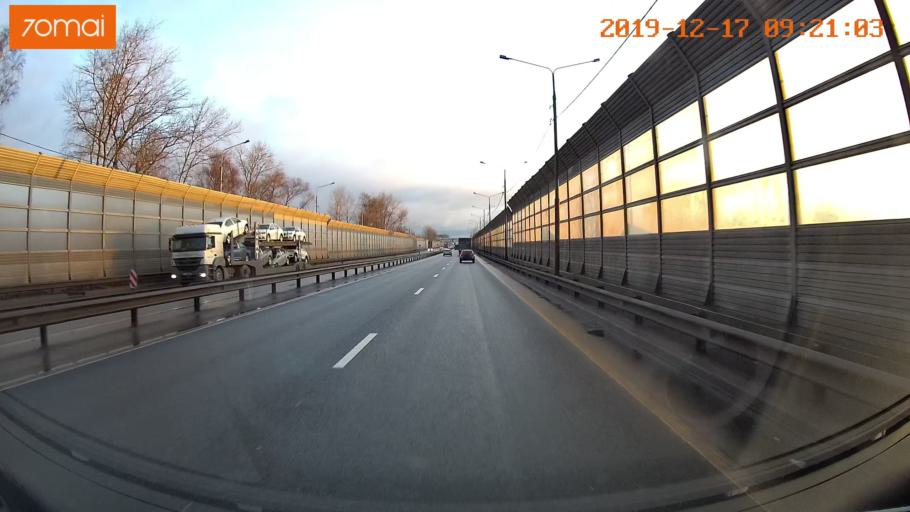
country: RU
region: Vladimir
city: Lakinsk
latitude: 56.0233
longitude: 39.9815
